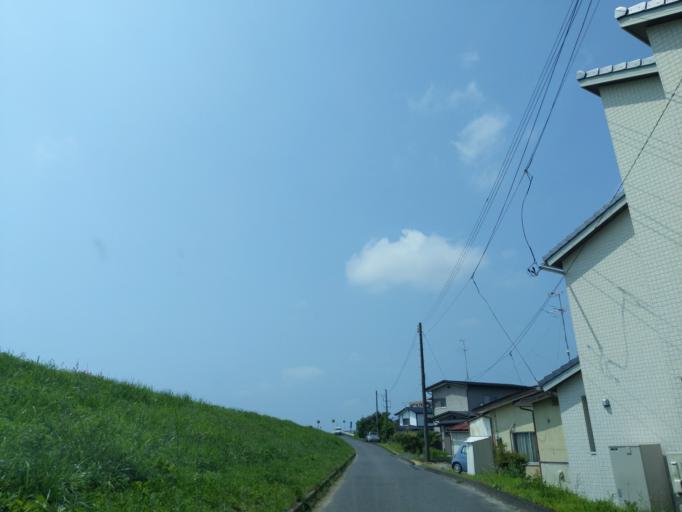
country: JP
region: Fukushima
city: Koriyama
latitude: 37.3825
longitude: 140.3929
